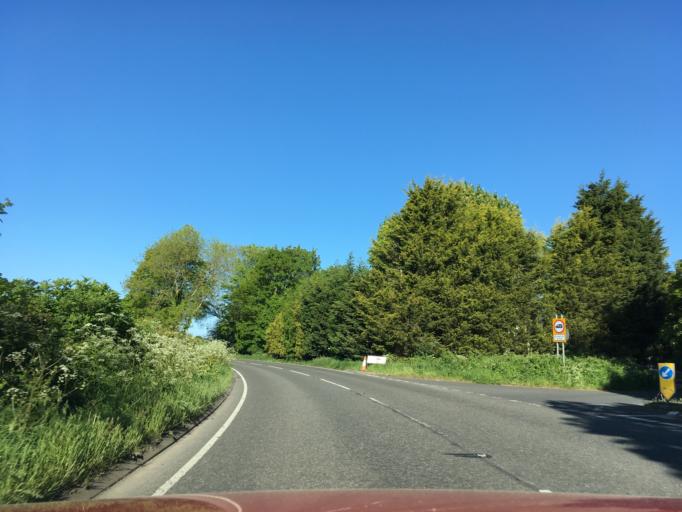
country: GB
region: England
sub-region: North Somerset
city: Nailsea
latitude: 51.4511
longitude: -2.7411
